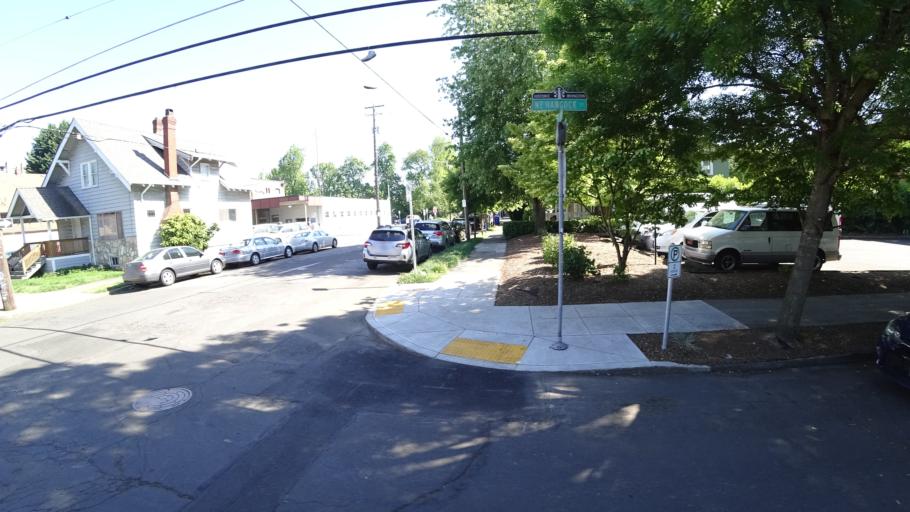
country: US
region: Oregon
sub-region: Multnomah County
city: Portland
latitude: 45.5365
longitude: -122.6577
